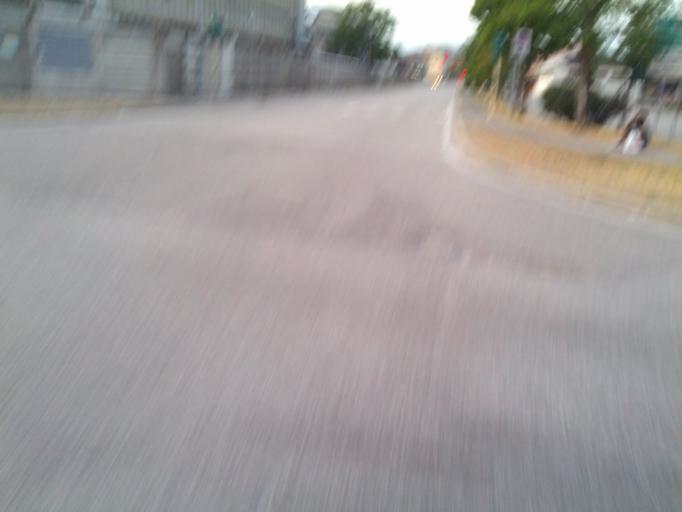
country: IT
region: Veneto
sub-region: Provincia di Verona
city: Beccacivetta-Azzano
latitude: 45.4059
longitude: 10.9618
